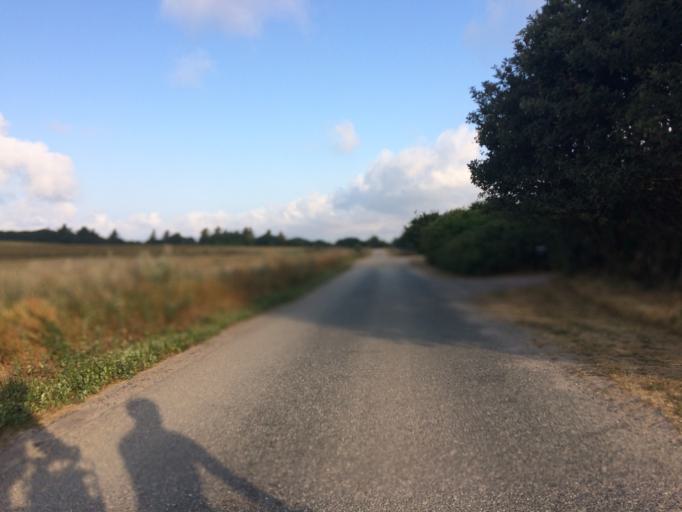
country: DK
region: Central Jutland
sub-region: Holstebro Kommune
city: Vinderup
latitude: 56.6057
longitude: 8.7026
